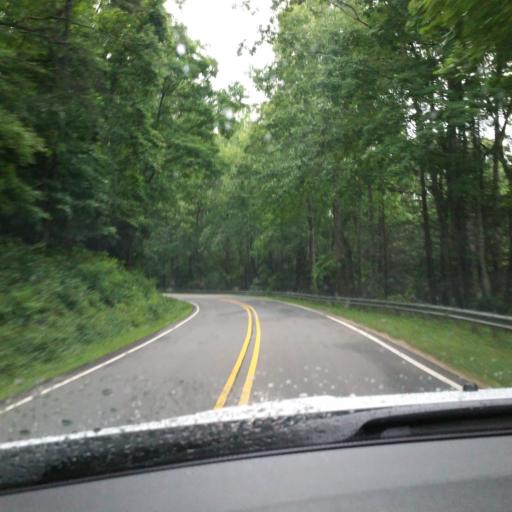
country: US
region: North Carolina
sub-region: Mitchell County
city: Spruce Pine
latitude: 35.7716
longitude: -82.1747
